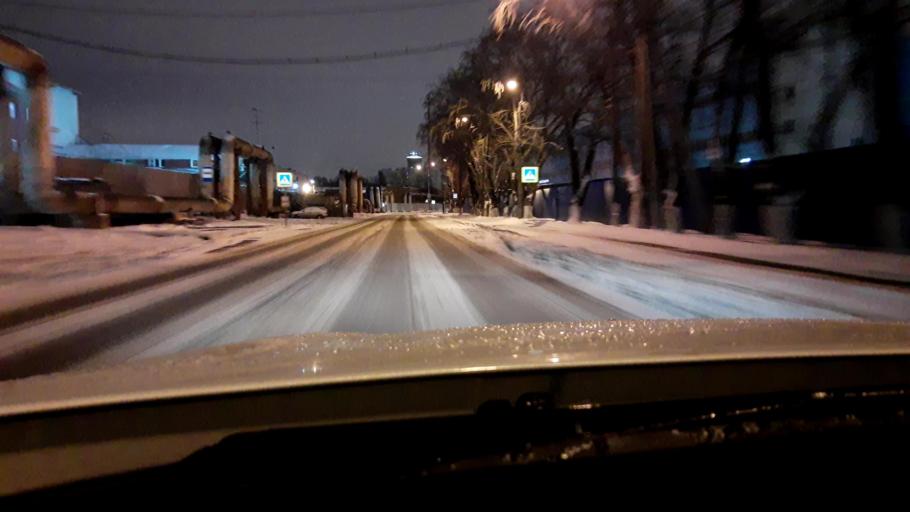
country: RU
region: Moscow
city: Khimki
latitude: 55.9042
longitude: 37.4346
